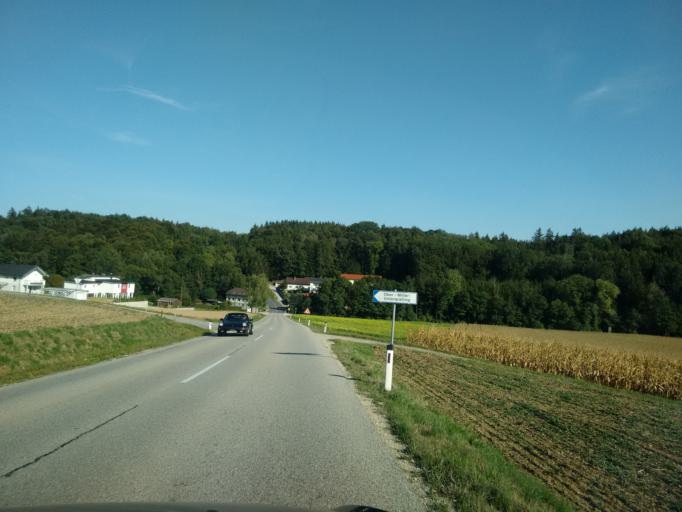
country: AT
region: Upper Austria
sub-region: Wels-Land
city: Marchtrenk
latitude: 48.1559
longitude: 14.1423
